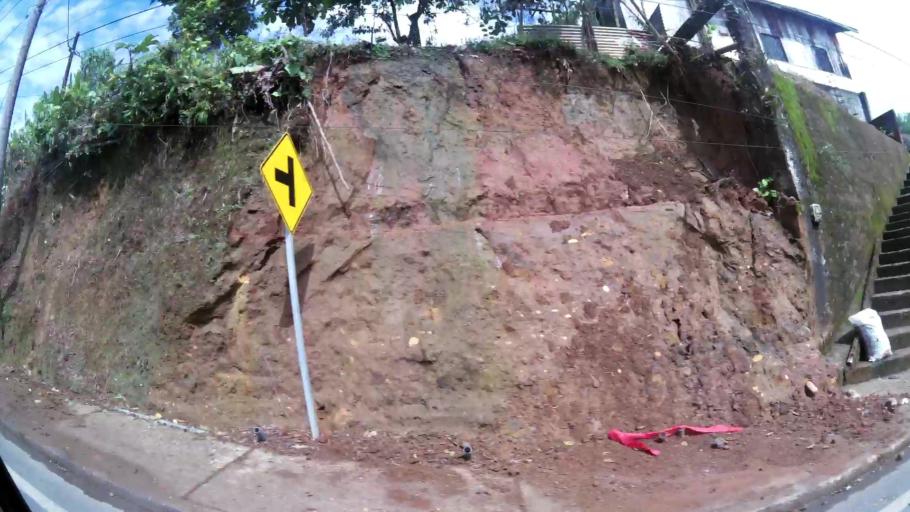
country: EC
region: Pastaza
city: Puyo
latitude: -1.4961
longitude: -78.0207
